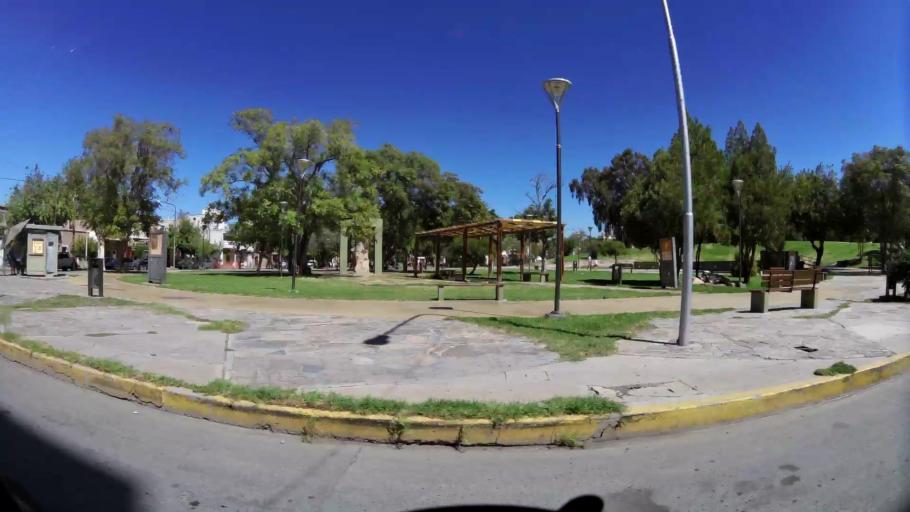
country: AR
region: San Juan
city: San Juan
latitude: -31.5434
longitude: -68.5238
